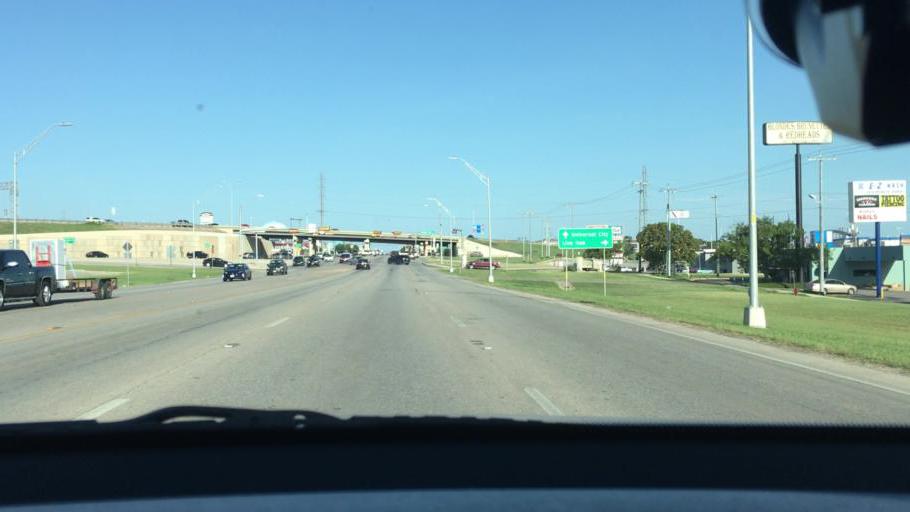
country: US
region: Texas
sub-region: Bexar County
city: Live Oak
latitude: 29.5617
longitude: -98.3302
